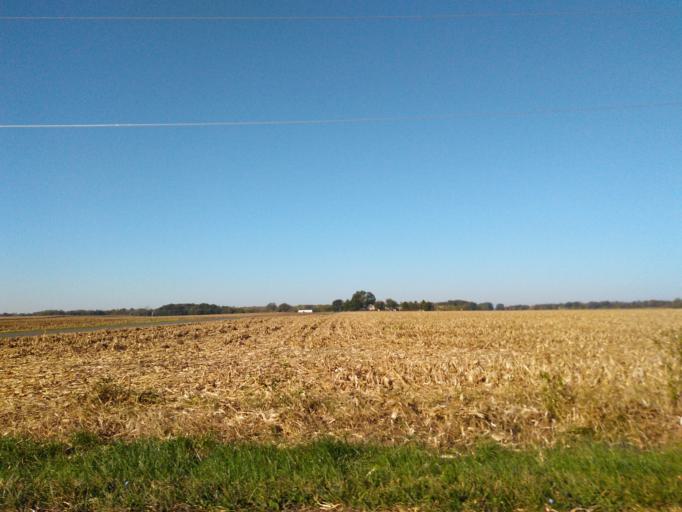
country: US
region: Illinois
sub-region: Madison County
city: Saint Jacob
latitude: 38.7578
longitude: -89.8007
